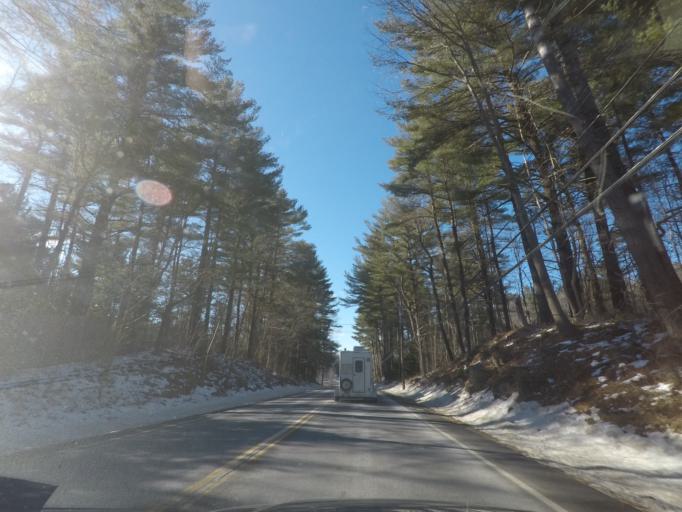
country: US
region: Massachusetts
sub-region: Berkshire County
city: Richmond
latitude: 42.4099
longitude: -73.4383
